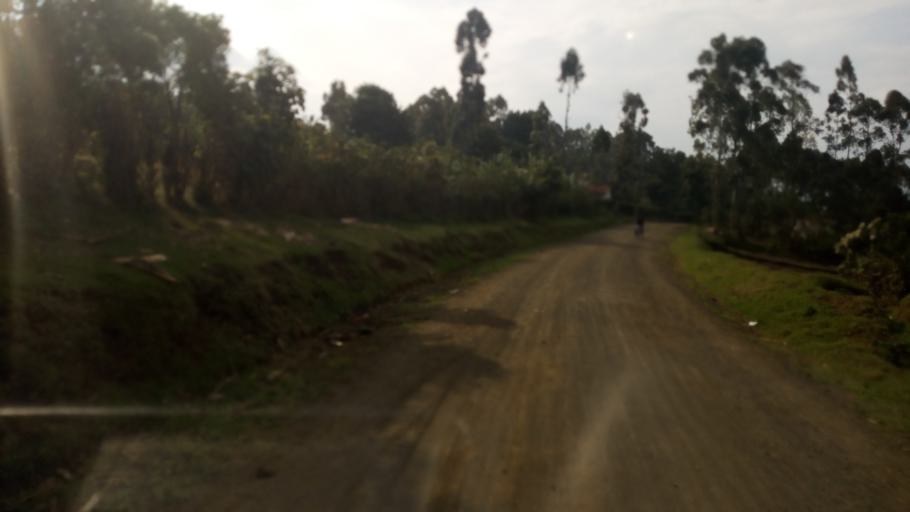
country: UG
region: Western Region
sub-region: Kisoro District
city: Kisoro
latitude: -1.2978
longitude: 29.7009
